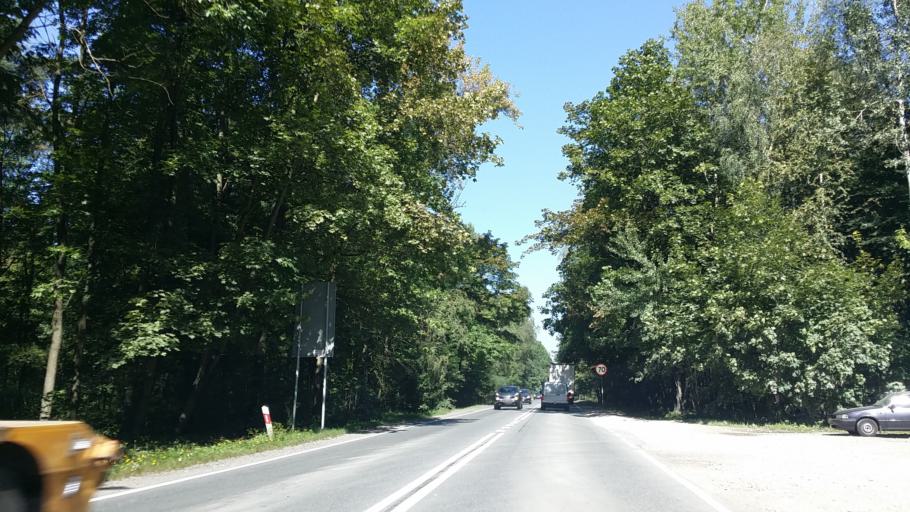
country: PL
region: Silesian Voivodeship
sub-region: Powiat bierunsko-ledzinski
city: Imielin
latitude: 50.1616
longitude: 19.1751
